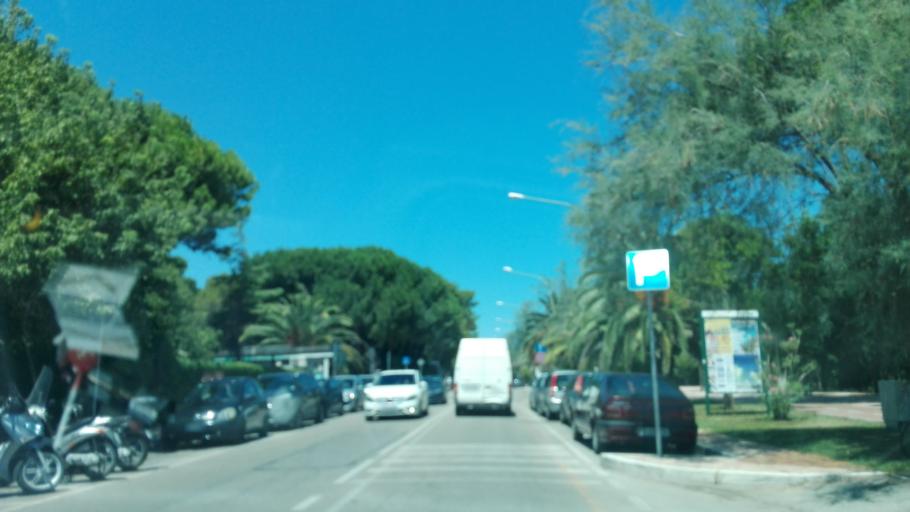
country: IT
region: Abruzzo
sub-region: Provincia di Pescara
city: Pescara
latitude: 42.4878
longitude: 14.1914
